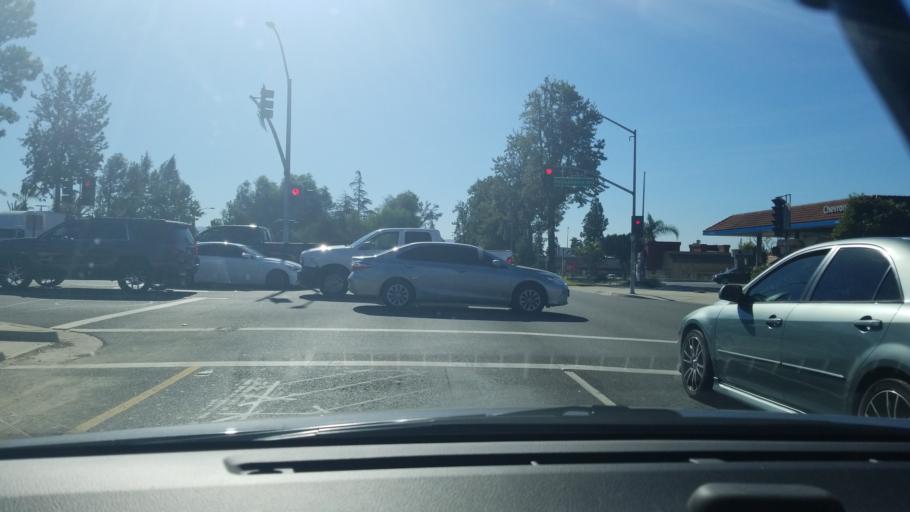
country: US
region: California
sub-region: San Bernardino County
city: Ontario
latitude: 34.0340
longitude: -117.6510
